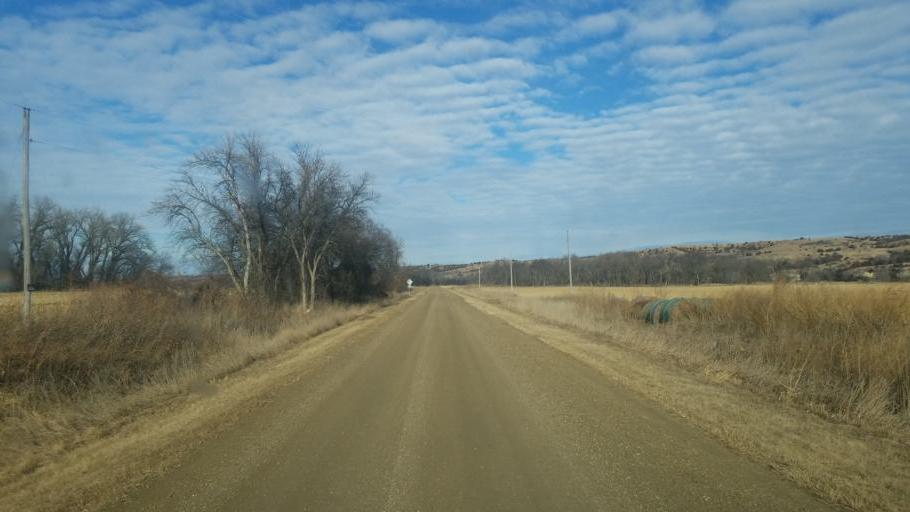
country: US
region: South Dakota
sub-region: Charles Mix County
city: Wagner
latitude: 42.9418
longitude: -98.4463
